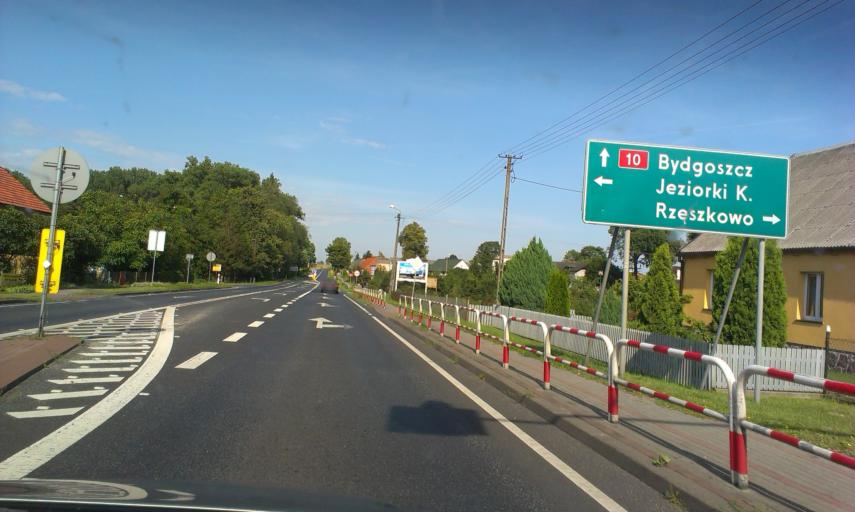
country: PL
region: Greater Poland Voivodeship
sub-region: Powiat pilski
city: Wyrzysk
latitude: 53.1603
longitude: 17.1928
